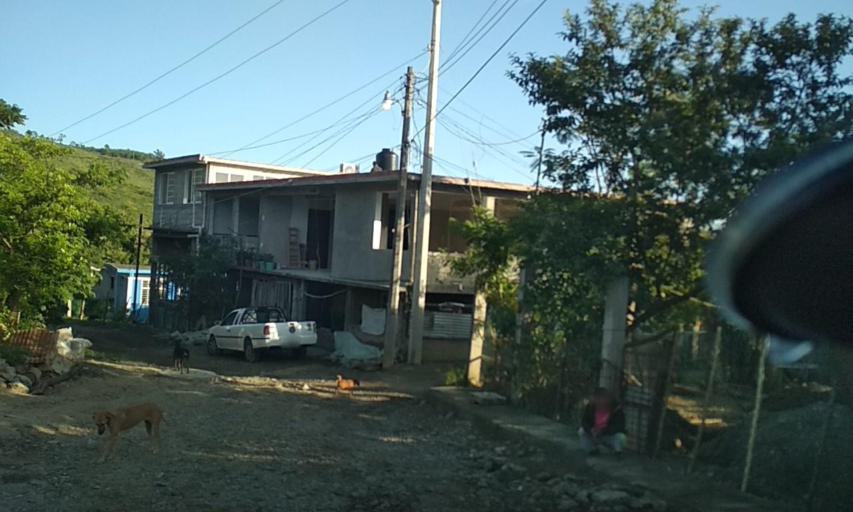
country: MX
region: Veracruz
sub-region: Poza Rica de Hidalgo
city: El Mollejon
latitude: 20.5438
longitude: -97.4070
